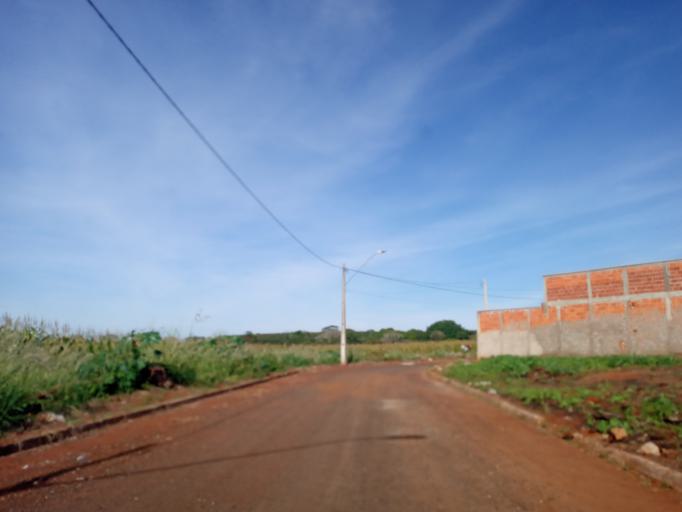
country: BR
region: Minas Gerais
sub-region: Ituiutaba
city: Ituiutaba
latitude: -18.9622
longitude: -49.4380
